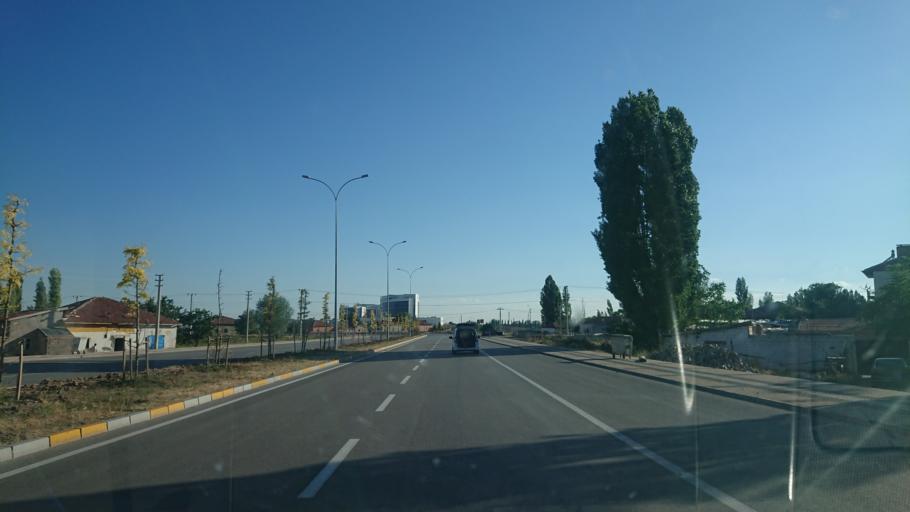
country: TR
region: Aksaray
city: Aksaray
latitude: 38.3795
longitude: 33.9891
